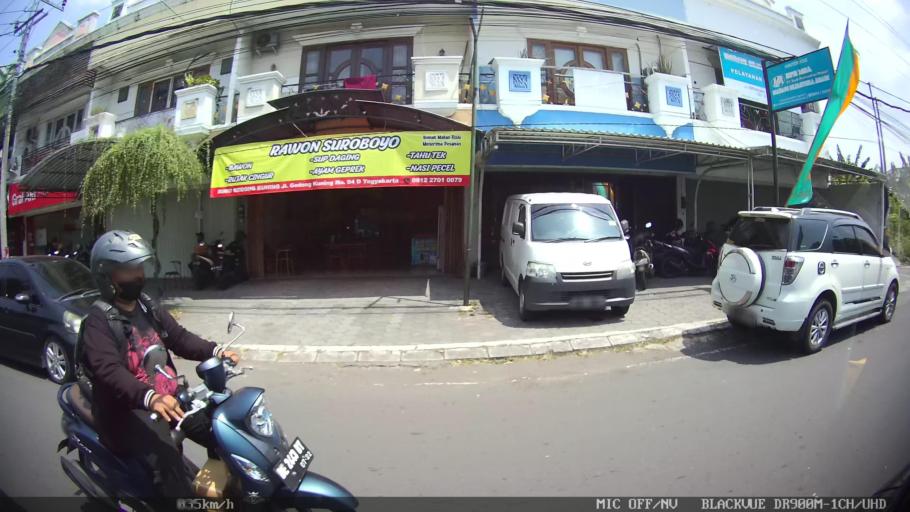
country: ID
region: Daerah Istimewa Yogyakarta
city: Yogyakarta
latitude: -7.8098
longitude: 110.4021
